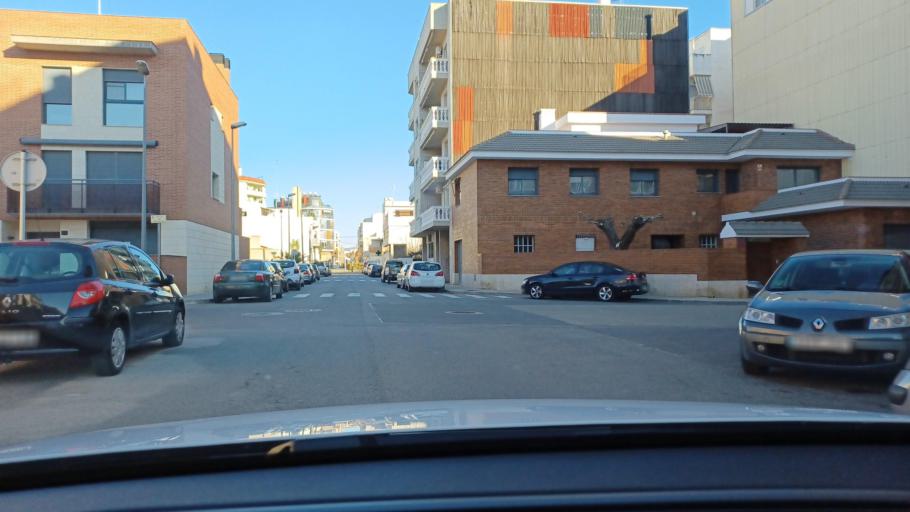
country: ES
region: Catalonia
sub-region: Provincia de Tarragona
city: Amposta
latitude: 40.7047
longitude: 0.5777
